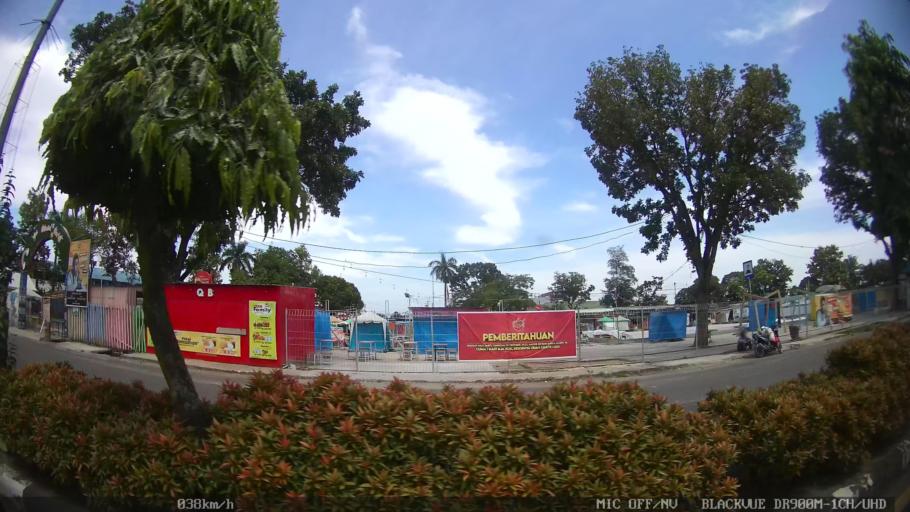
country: ID
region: North Sumatra
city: Binjai
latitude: 3.6166
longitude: 98.4981
